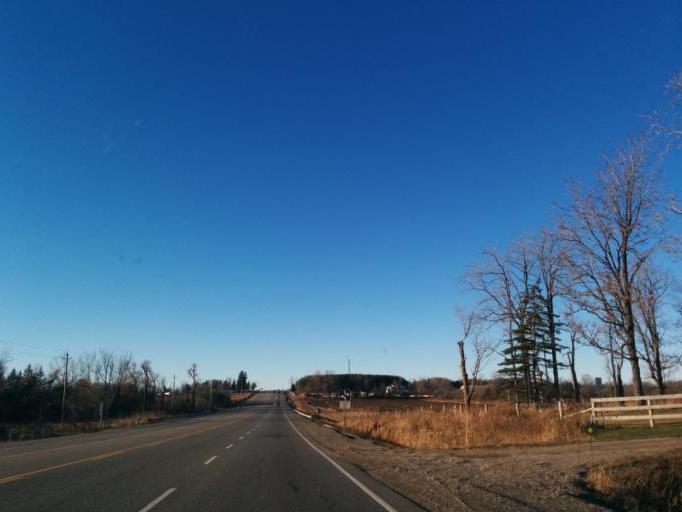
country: CA
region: Ontario
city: Orangeville
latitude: 43.8734
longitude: -80.0136
